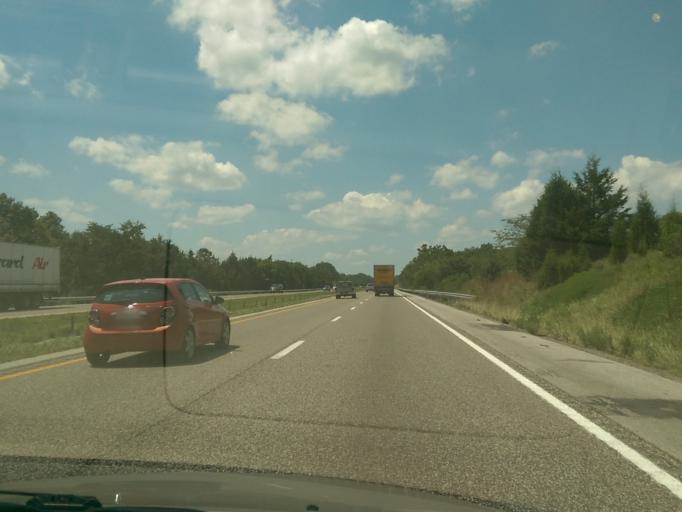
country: US
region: Missouri
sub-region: Boone County
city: Columbia
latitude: 38.9722
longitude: -92.4449
